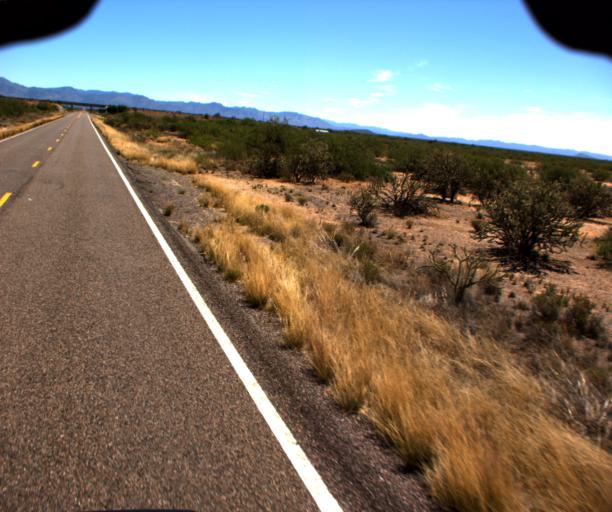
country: US
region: Arizona
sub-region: Yavapai County
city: Congress
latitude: 34.1216
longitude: -112.9551
